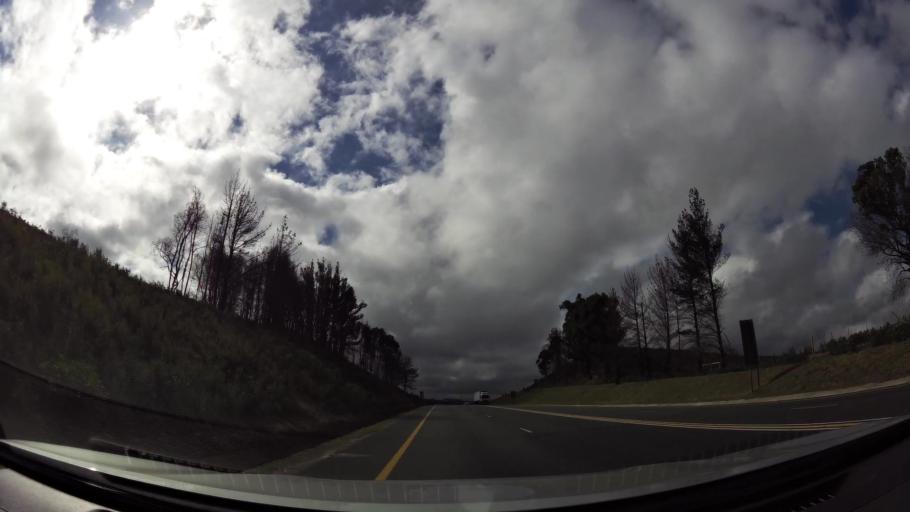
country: ZA
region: Western Cape
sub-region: Eden District Municipality
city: Knysna
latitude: -34.0370
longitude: 23.1226
